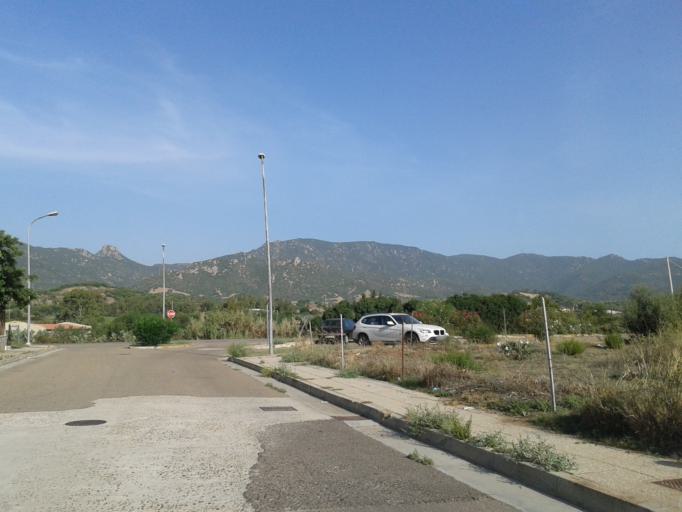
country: IT
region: Sardinia
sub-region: Provincia di Cagliari
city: Villasimius
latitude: 39.1507
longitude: 9.5150
